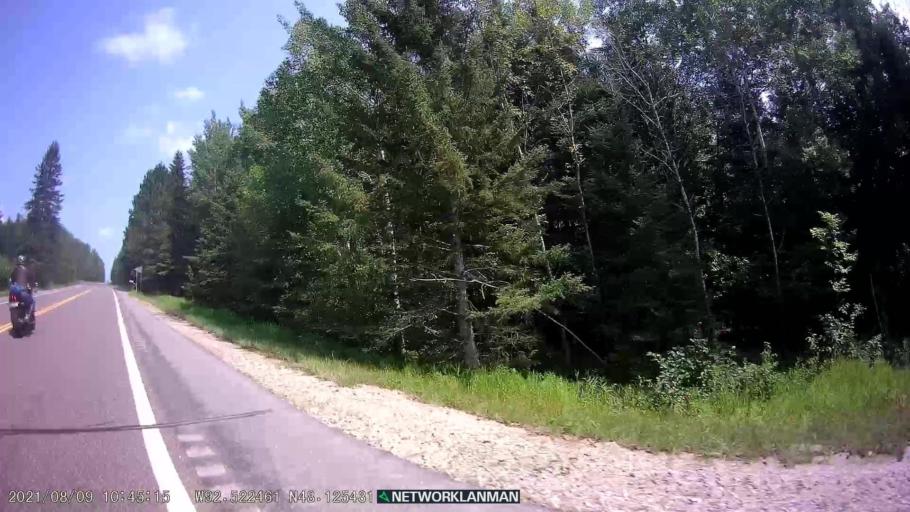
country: US
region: Minnesota
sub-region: Saint Louis County
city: Parkville
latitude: 48.1257
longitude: -92.5224
